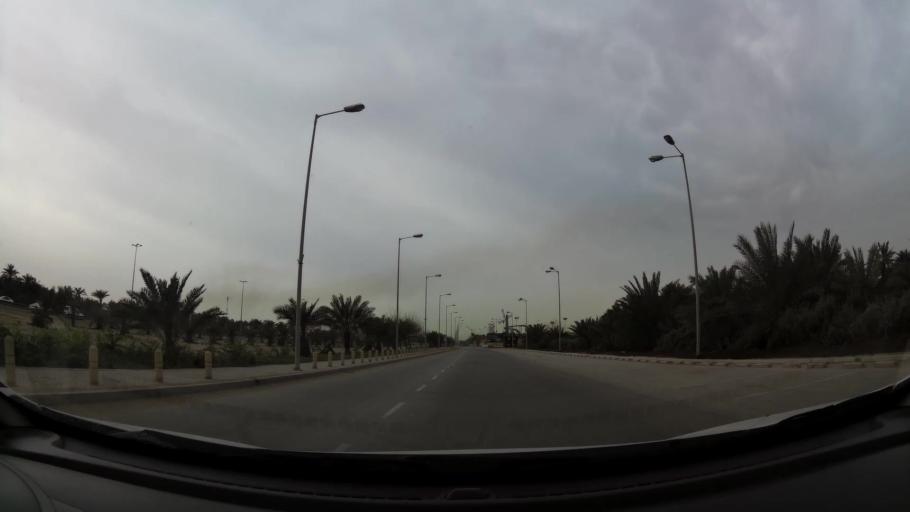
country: BH
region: Manama
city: Jidd Hafs
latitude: 26.1981
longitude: 50.5497
